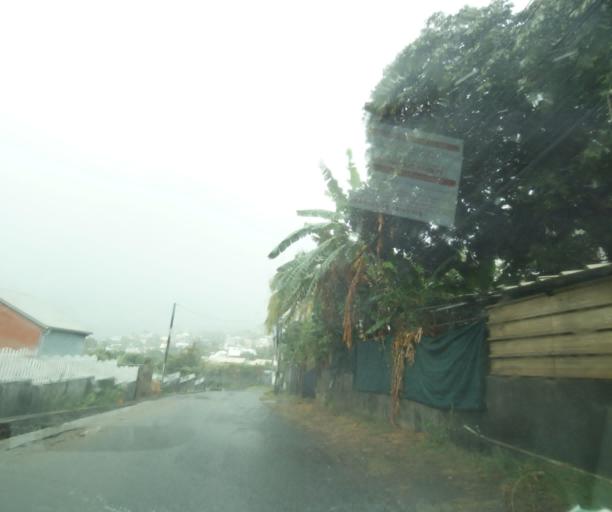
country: RE
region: Reunion
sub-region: Reunion
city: La Possession
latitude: -20.9861
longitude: 55.3244
